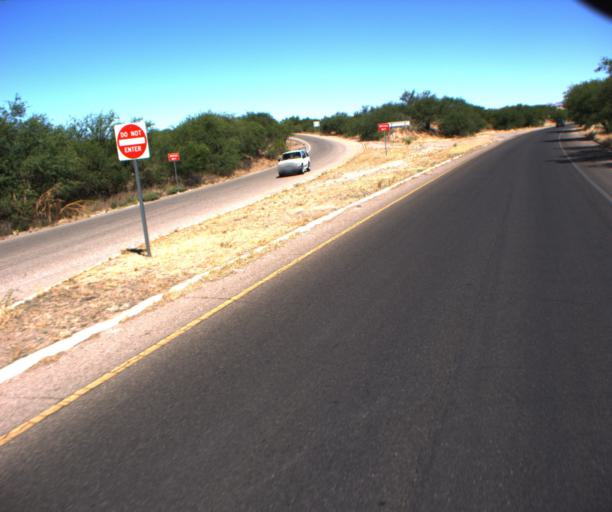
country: US
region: Arizona
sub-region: Santa Cruz County
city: Nogales
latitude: 31.3939
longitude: -110.9562
